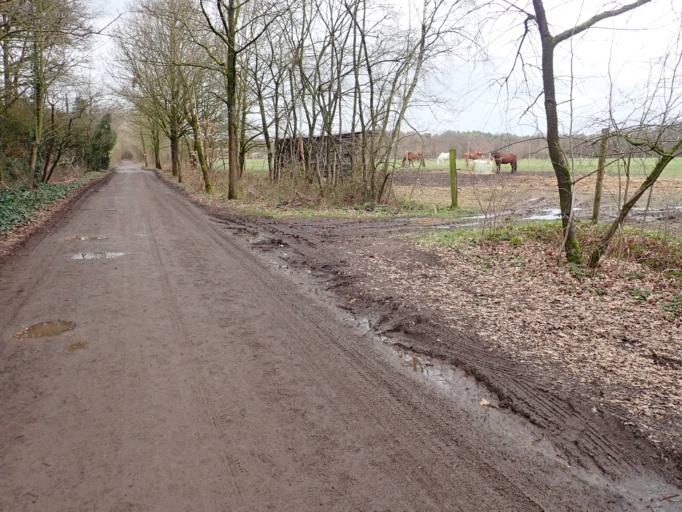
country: BE
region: Flanders
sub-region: Provincie Antwerpen
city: Schilde
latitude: 51.2935
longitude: 4.6060
